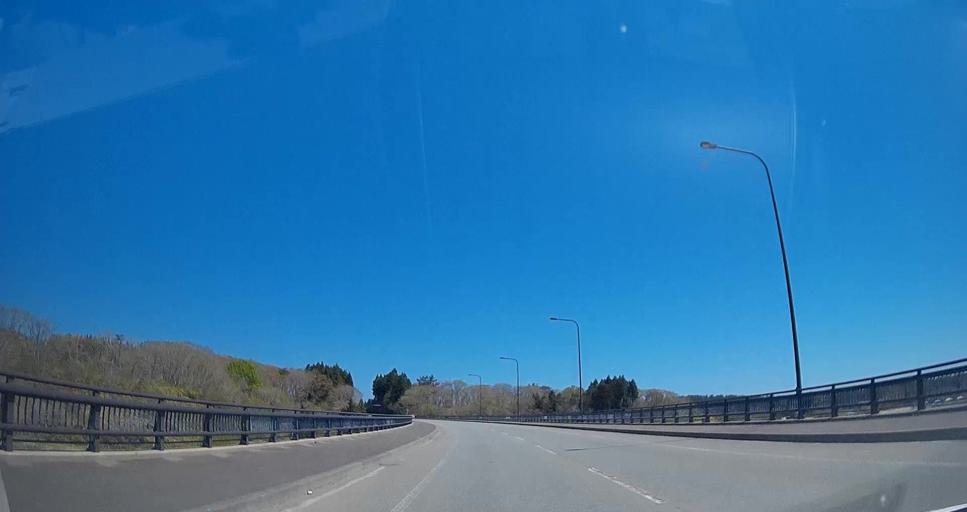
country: JP
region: Aomori
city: Misawa
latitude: 40.9821
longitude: 141.3635
